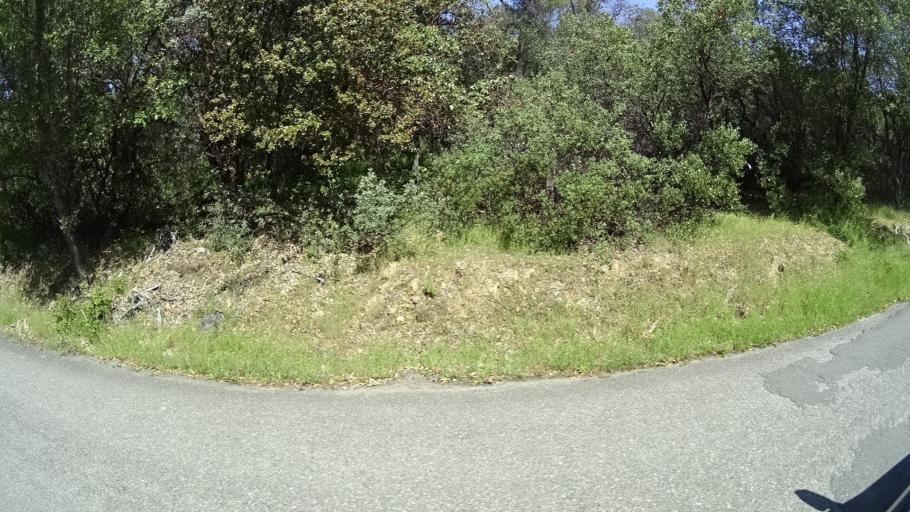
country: US
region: California
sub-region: Humboldt County
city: Redway
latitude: 40.1766
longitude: -123.5983
